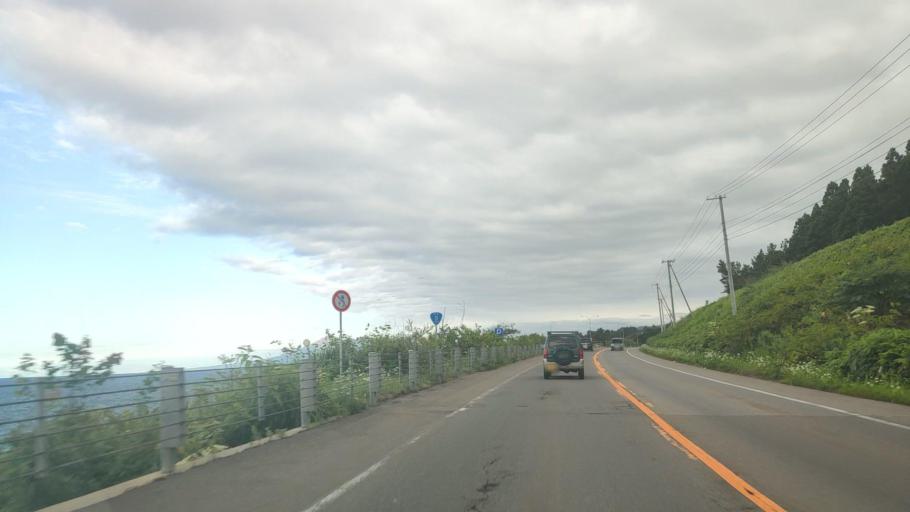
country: JP
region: Hokkaido
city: Nanae
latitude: 42.2065
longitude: 140.4044
